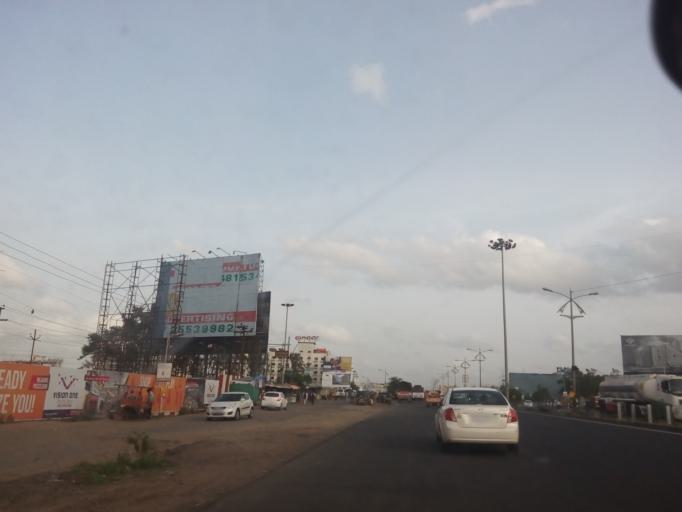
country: IN
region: Maharashtra
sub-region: Pune Division
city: Pimpri
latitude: 18.6088
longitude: 73.7511
